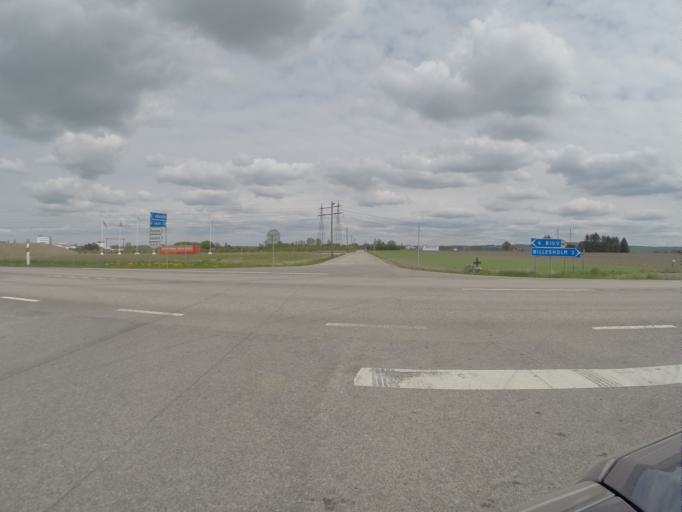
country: SE
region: Skane
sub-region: Bjuvs Kommun
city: Bjuv
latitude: 56.0661
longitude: 12.9442
